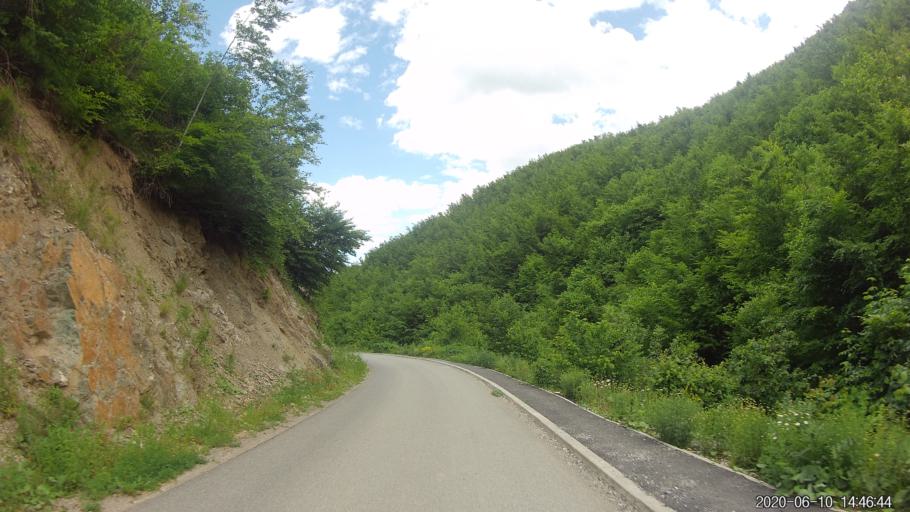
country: XK
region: Prizren
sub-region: Komuna e Therandes
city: Budakovo
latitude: 42.3844
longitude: 20.9587
